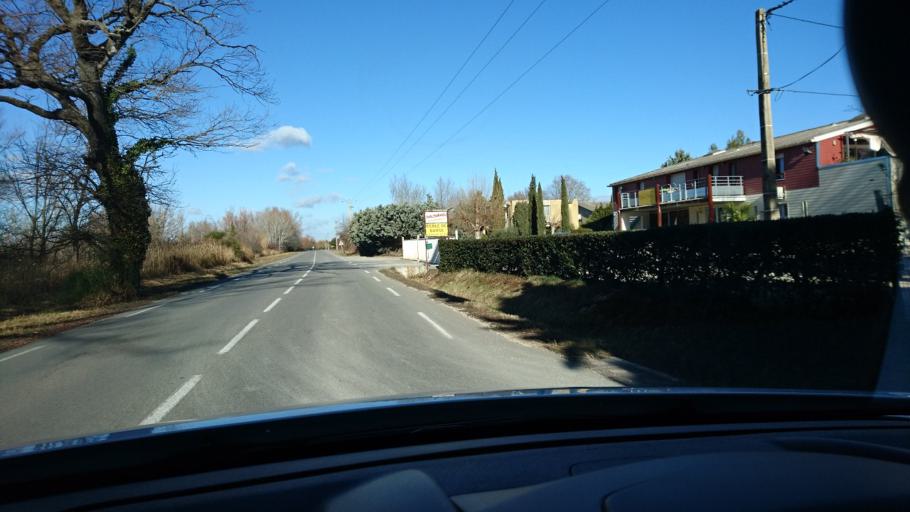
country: FR
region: Provence-Alpes-Cote d'Azur
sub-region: Departement du Vaucluse
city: Morieres-les-Avignon
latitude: 43.9192
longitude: 4.9061
